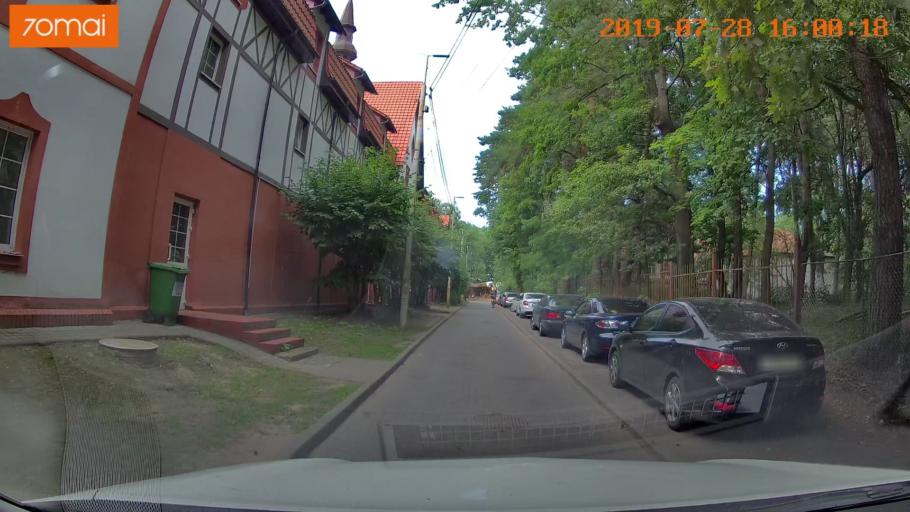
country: RU
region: Kaliningrad
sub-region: Gorod Svetlogorsk
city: Svetlogorsk
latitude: 54.9433
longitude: 20.1567
